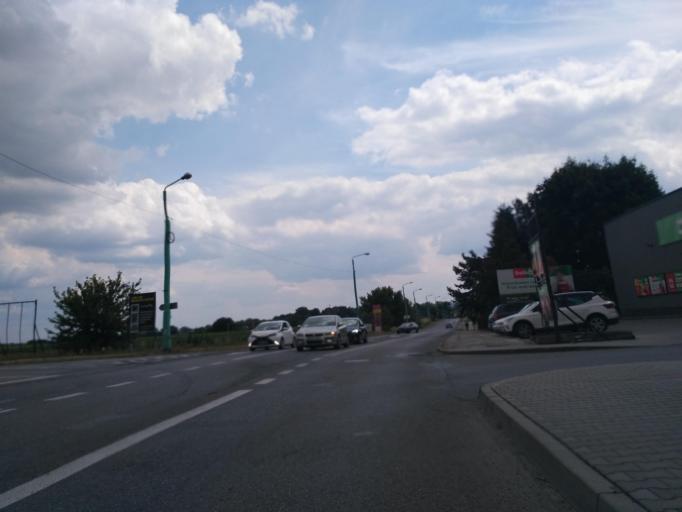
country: PL
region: Subcarpathian Voivodeship
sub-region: Powiat debicki
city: Zyrakow
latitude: 50.0635
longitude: 21.3642
